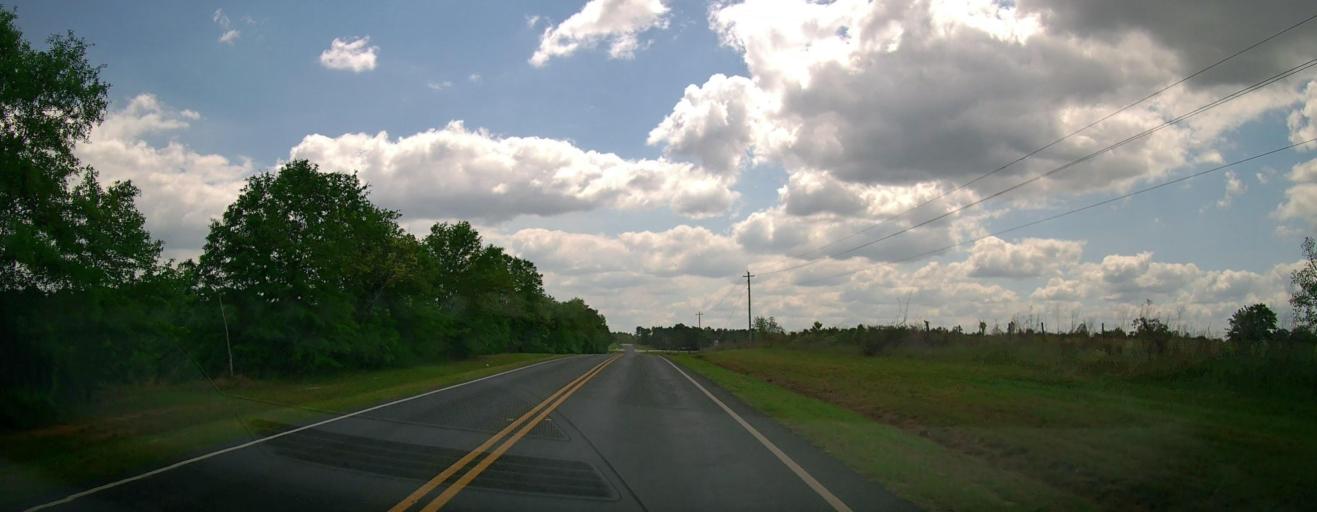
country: US
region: Georgia
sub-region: Treutlen County
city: Soperton
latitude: 32.4411
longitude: -82.6068
